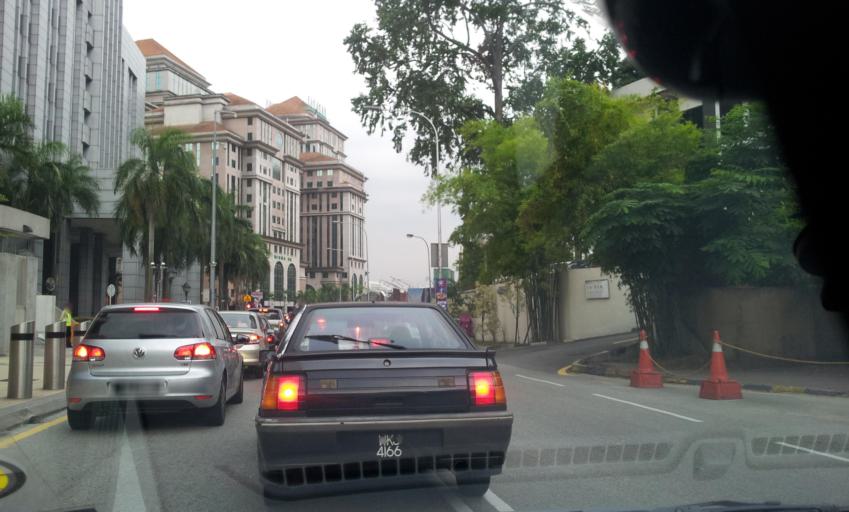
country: MY
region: Kuala Lumpur
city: Kuala Lumpur
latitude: 3.1603
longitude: 101.7109
